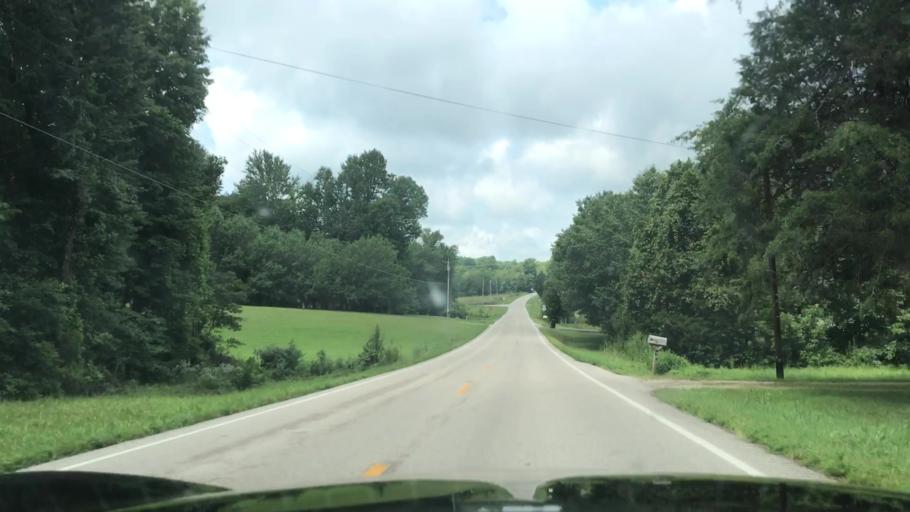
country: US
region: Kentucky
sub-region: Butler County
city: Morgantown
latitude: 37.1727
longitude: -86.8157
